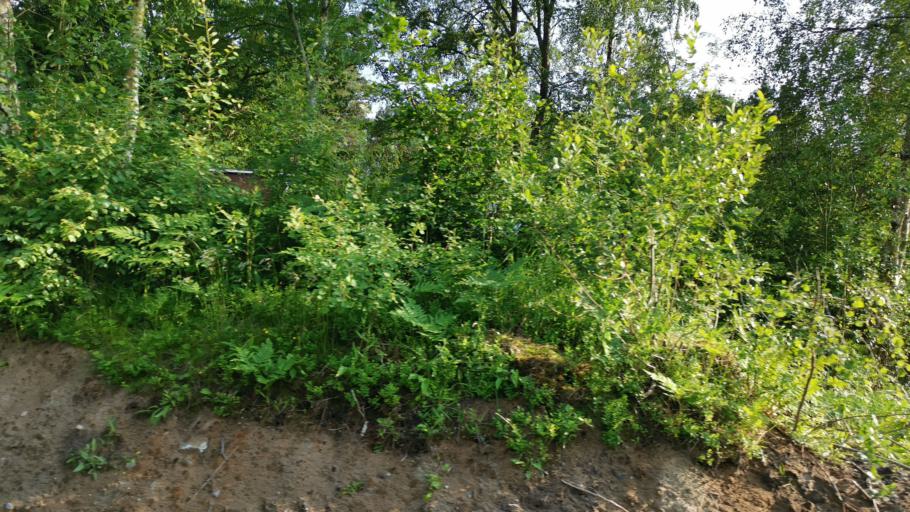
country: SE
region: Vaestra Goetaland
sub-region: Orust
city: Henan
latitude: 58.2882
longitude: 11.6500
